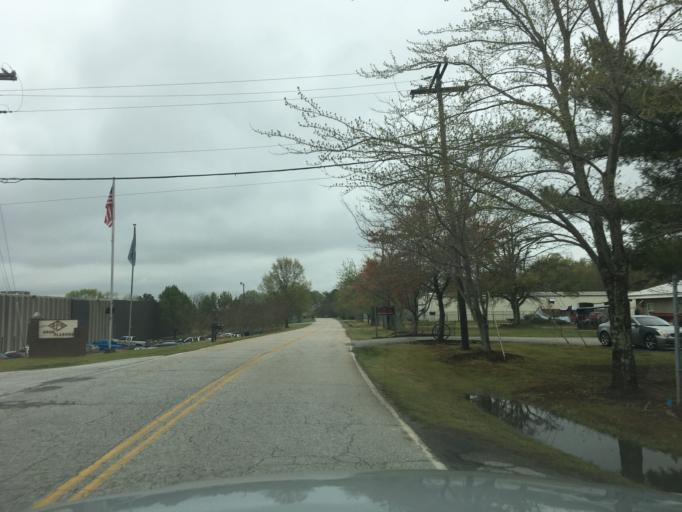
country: US
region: South Carolina
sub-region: Spartanburg County
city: Southern Shops
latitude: 34.9757
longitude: -82.0024
